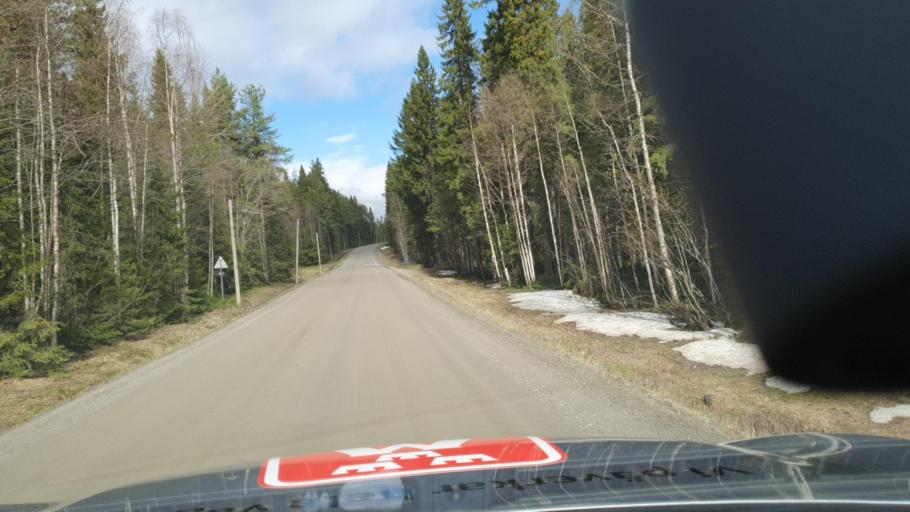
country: SE
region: Vaesterbotten
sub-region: Bjurholms Kommun
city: Bjurholm
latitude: 63.6986
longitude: 18.8967
